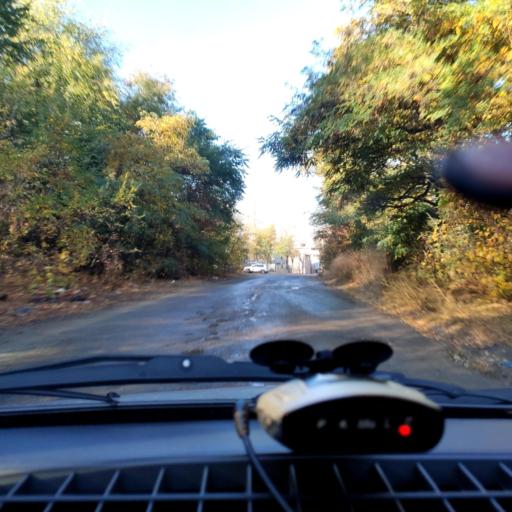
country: RU
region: Voronezj
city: Voronezh
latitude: 51.6690
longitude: 39.1401
